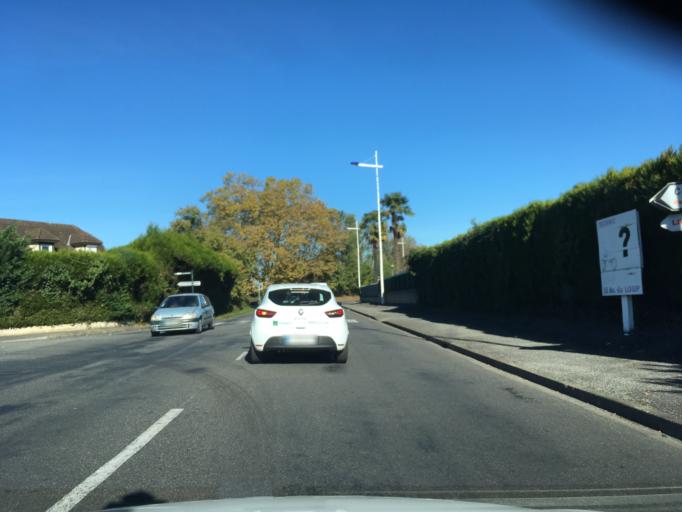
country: FR
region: Aquitaine
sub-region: Departement des Pyrenees-Atlantiques
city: Idron
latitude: 43.3030
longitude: -0.3296
